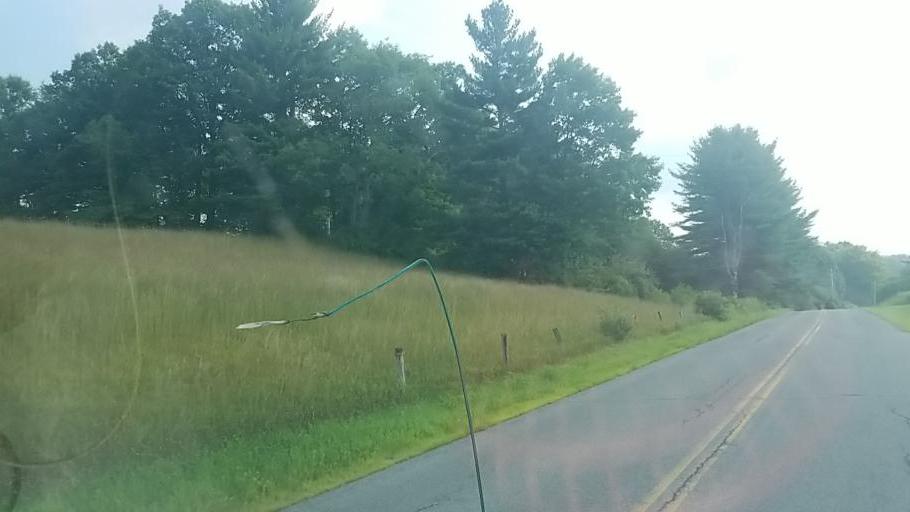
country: US
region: New York
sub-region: Fulton County
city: Broadalbin
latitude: 43.0705
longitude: -74.2401
